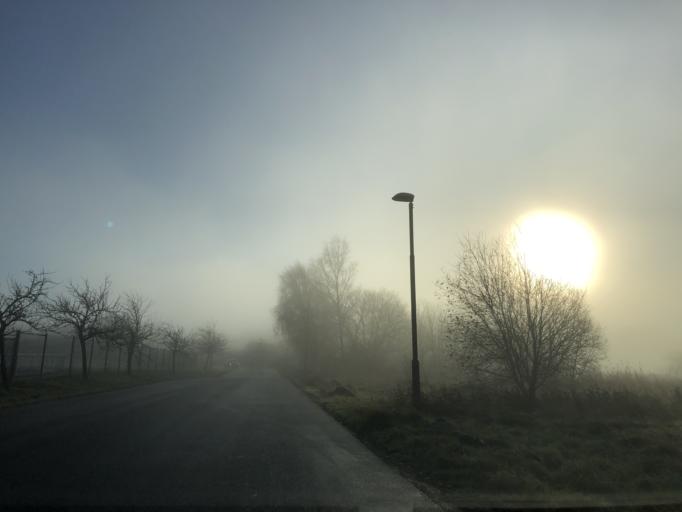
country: SE
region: Vaestra Goetaland
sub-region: Goteborg
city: Hammarkullen
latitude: 57.7927
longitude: 12.0513
